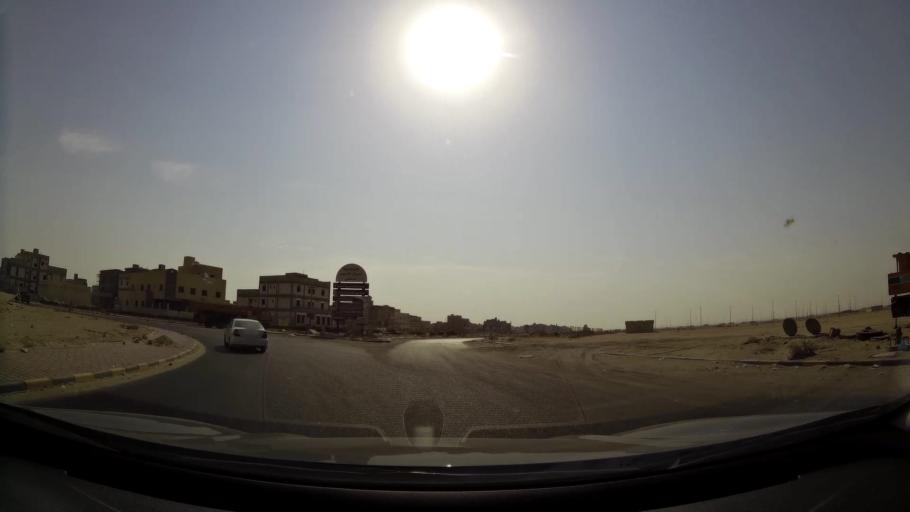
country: KW
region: Al Ahmadi
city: Al Wafrah
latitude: 28.7747
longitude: 48.0518
